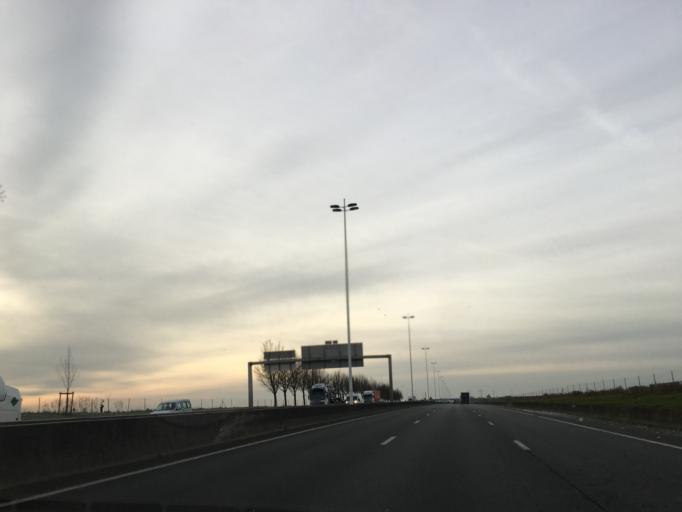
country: FR
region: Nord-Pas-de-Calais
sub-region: Departement du Pas-de-Calais
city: Noyelles-Godault
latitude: 50.4028
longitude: 2.9834
